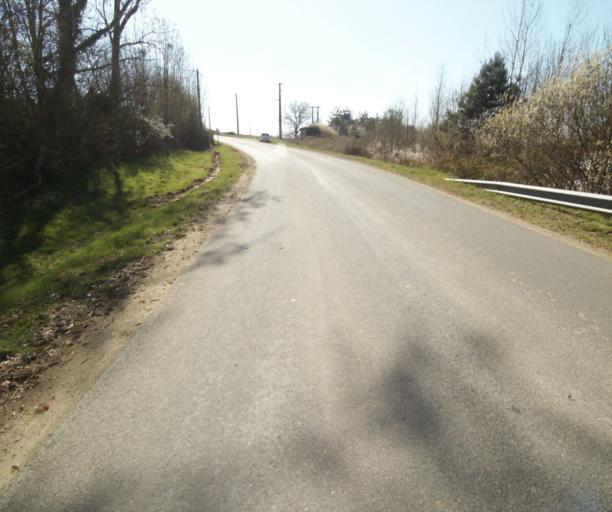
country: FR
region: Limousin
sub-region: Departement de la Correze
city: Saint-Mexant
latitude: 45.2829
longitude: 1.6196
